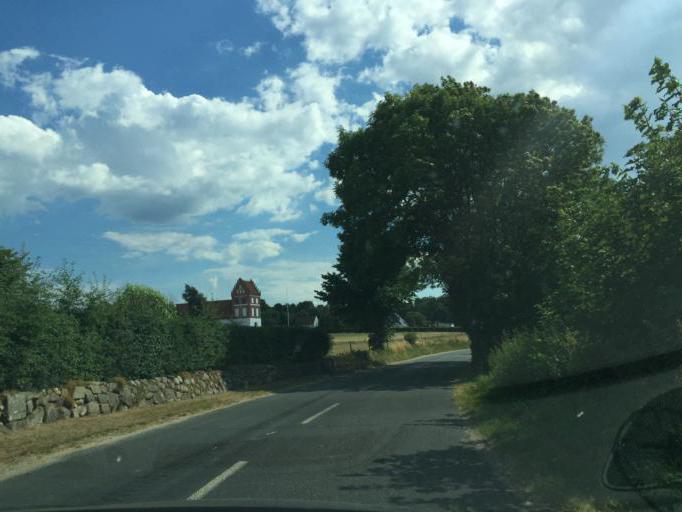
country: DK
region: South Denmark
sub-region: Assens Kommune
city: Harby
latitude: 55.1432
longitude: 10.0205
